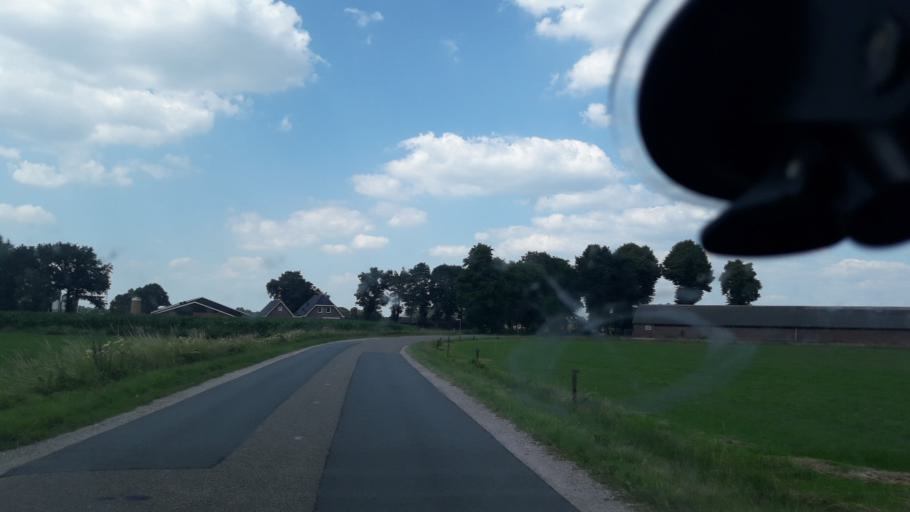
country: NL
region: Gelderland
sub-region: Gemeente Ede
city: Lunteren
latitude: 52.1254
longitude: 5.6349
